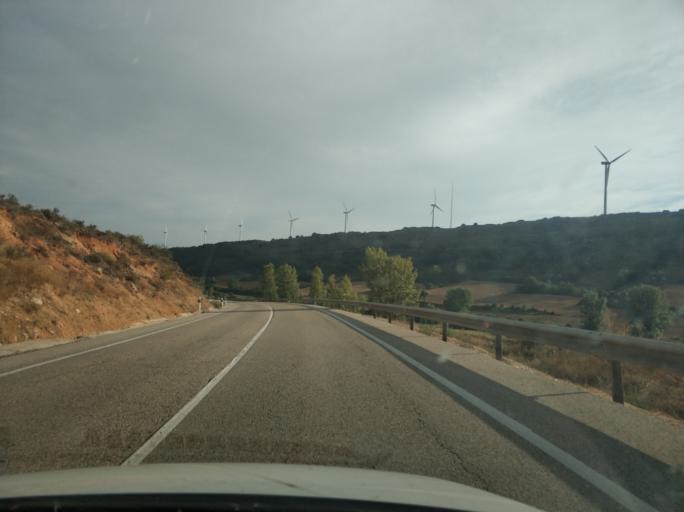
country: ES
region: Castille and Leon
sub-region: Provincia de Burgos
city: Montorio
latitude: 42.5872
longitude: -3.7857
